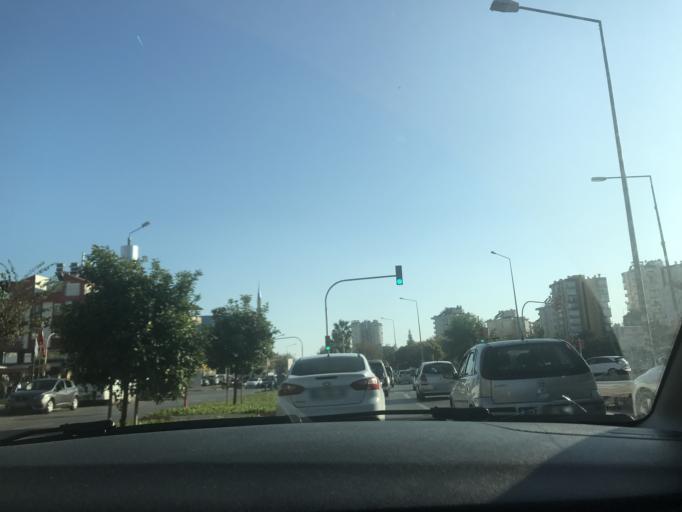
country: TR
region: Antalya
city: Antalya
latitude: 36.8842
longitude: 30.6481
